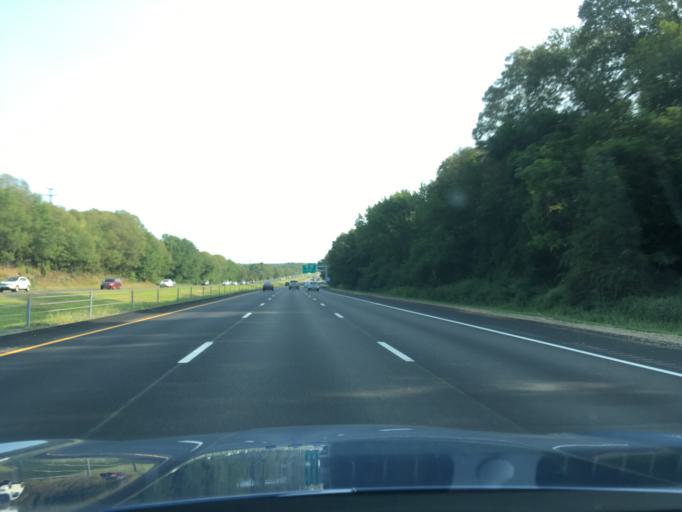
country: US
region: Rhode Island
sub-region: Kent County
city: East Greenwich
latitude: 41.6454
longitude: -71.4880
